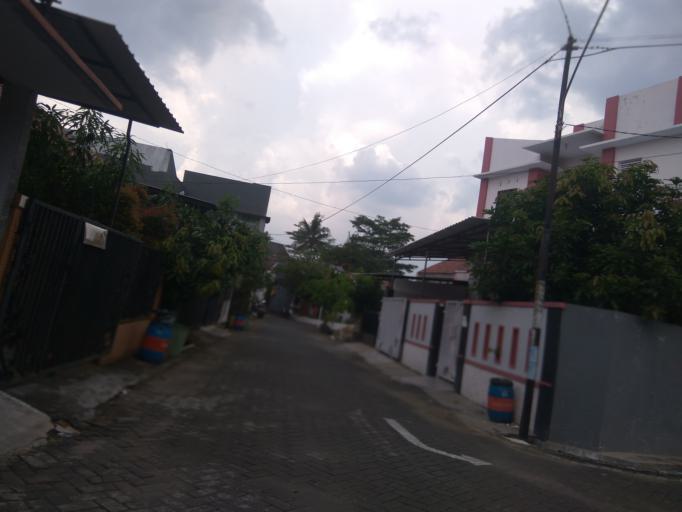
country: ID
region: Central Java
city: Semarang
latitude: -7.0658
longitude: 110.4453
